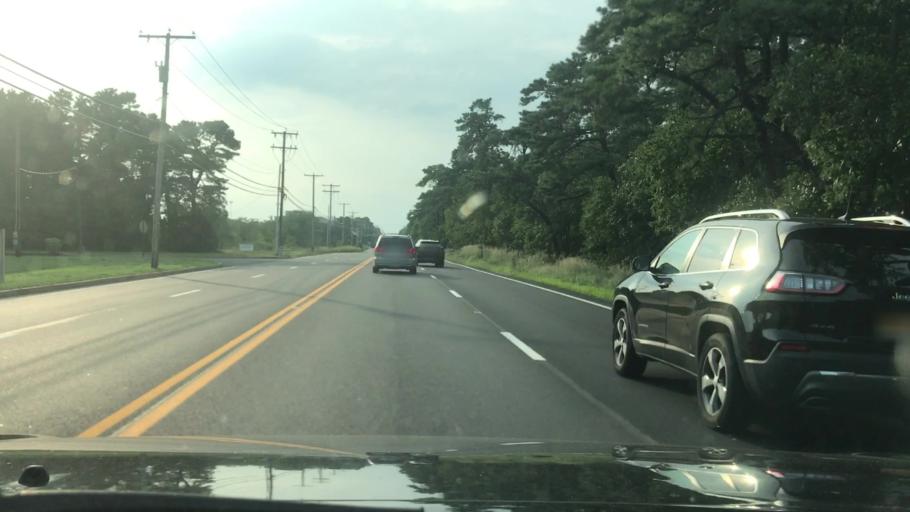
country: US
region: New Jersey
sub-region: Ocean County
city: Leisure Village
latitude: 40.0722
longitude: -74.1754
